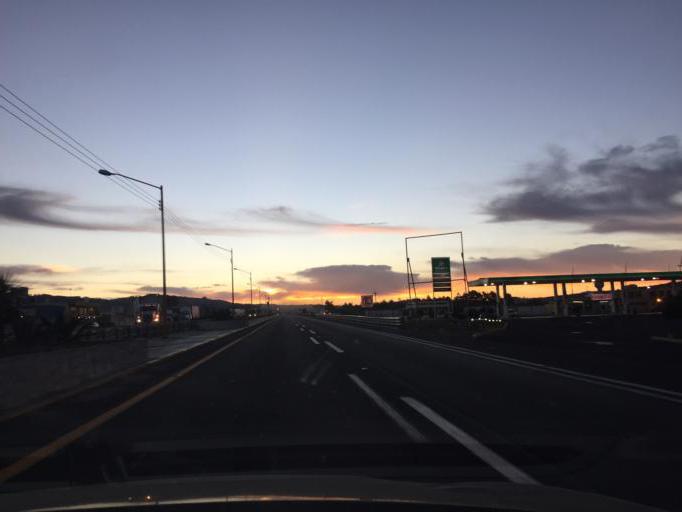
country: MX
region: Puebla
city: San Jose Esperanza
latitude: 18.8665
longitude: -97.3768
